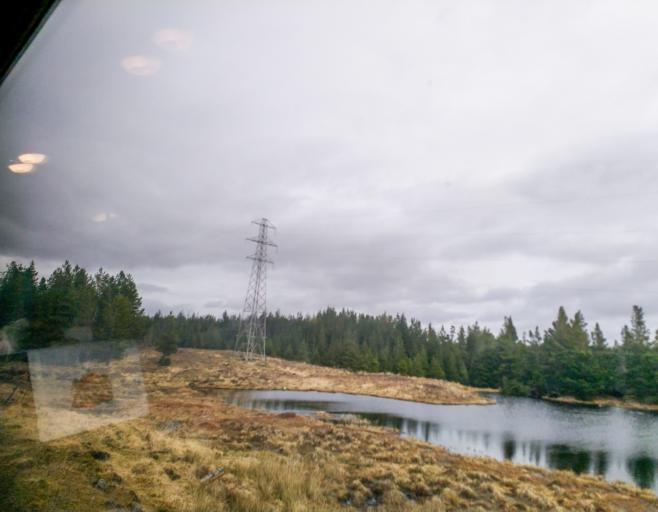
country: GB
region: Scotland
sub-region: Highland
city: Spean Bridge
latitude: 56.6562
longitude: -4.5647
